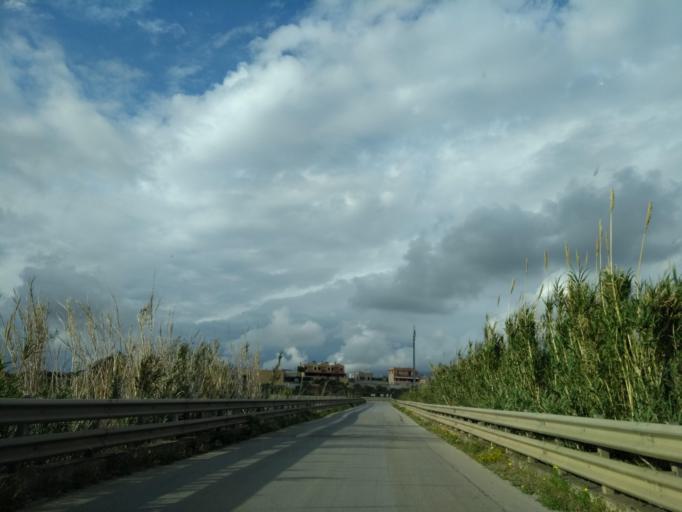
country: IT
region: Sicily
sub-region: Trapani
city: Marausa
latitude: 37.9473
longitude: 12.5137
